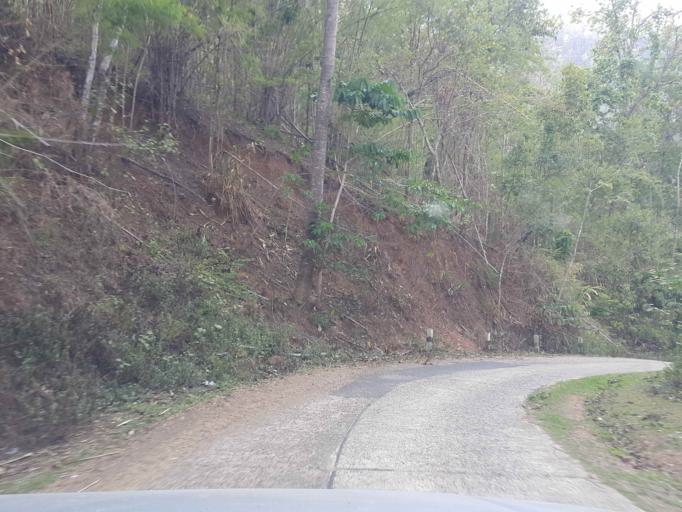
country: TH
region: Chiang Mai
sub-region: Amphoe Chiang Dao
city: Chiang Dao
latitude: 19.3872
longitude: 98.7697
